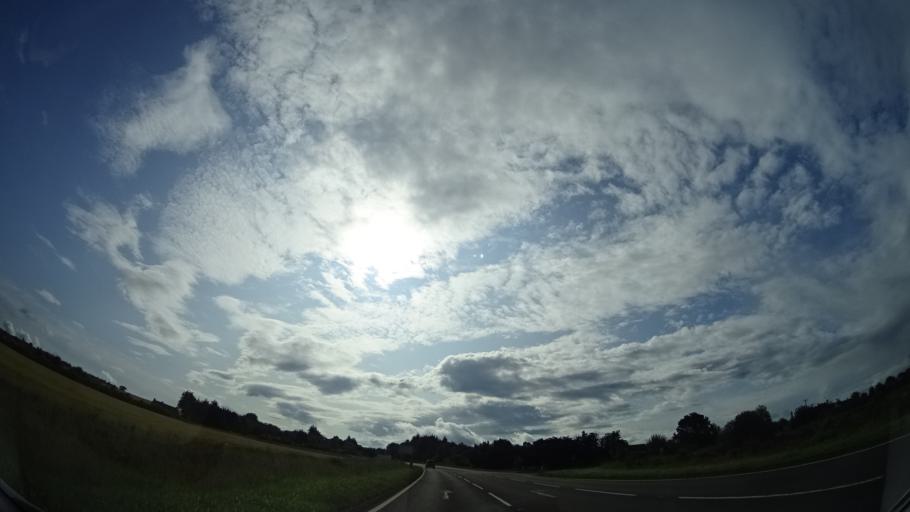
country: GB
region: Scotland
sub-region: Highland
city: Conon Bridge
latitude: 57.5519
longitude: -4.4083
